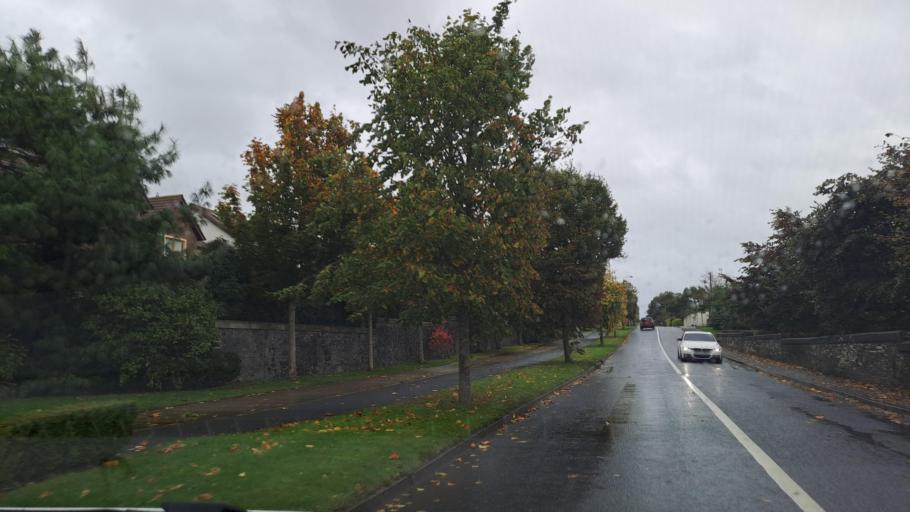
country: IE
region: Leinster
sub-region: Lu
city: Blackrock
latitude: 53.9643
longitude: -6.3913
